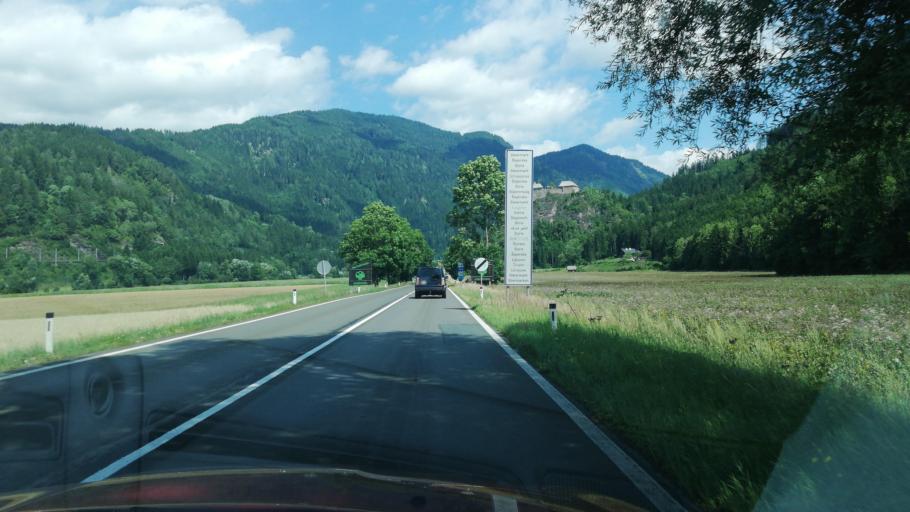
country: AT
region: Styria
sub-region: Politischer Bezirk Murau
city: Durnstein in der Steiermark
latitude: 46.9822
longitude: 14.3914
